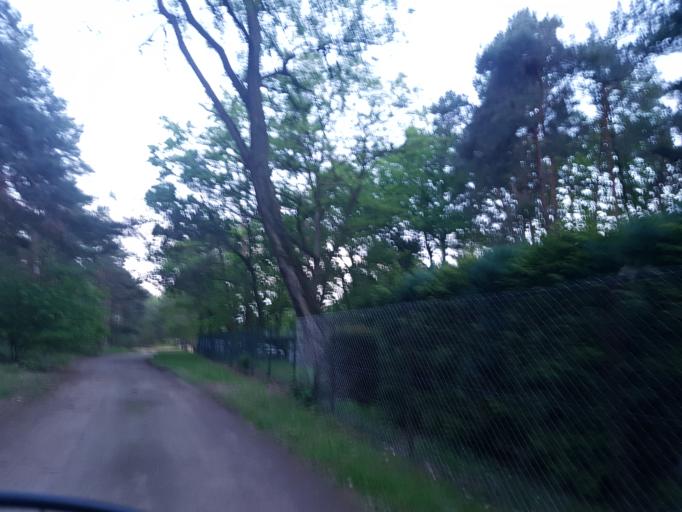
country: DE
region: Brandenburg
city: Bad Liebenwerda
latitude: 51.5526
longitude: 13.3707
